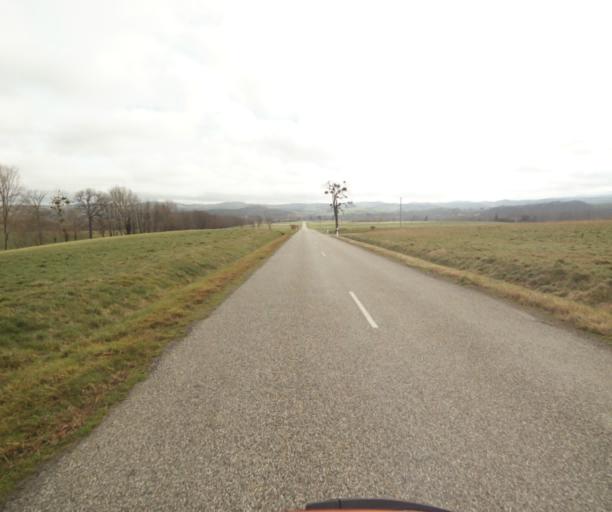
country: FR
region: Midi-Pyrenees
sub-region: Departement de l'Ariege
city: Pamiers
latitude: 43.1099
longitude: 1.5268
